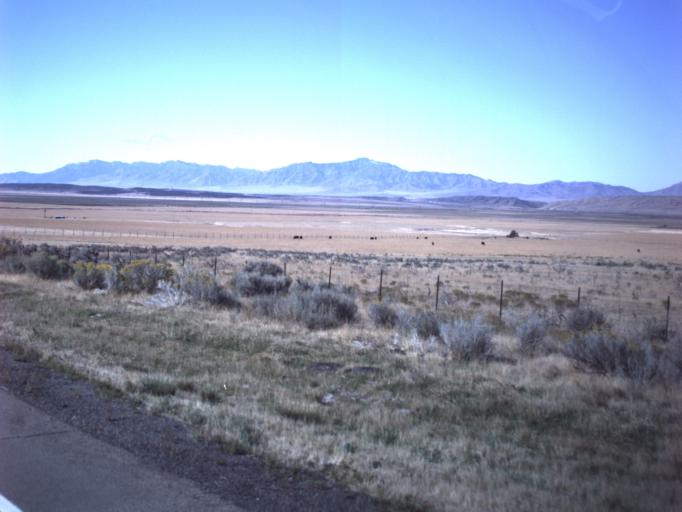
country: US
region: Utah
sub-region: Juab County
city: Nephi
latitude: 39.5049
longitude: -111.8731
